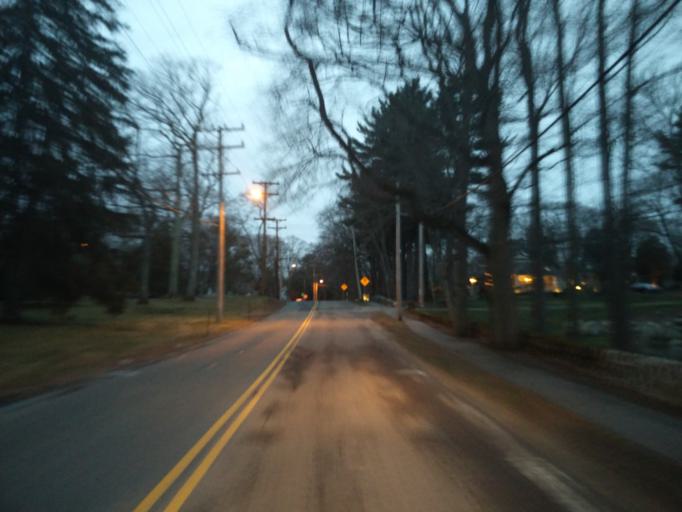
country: US
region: Massachusetts
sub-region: Plymouth County
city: Hingham
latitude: 42.2424
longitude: -70.8667
